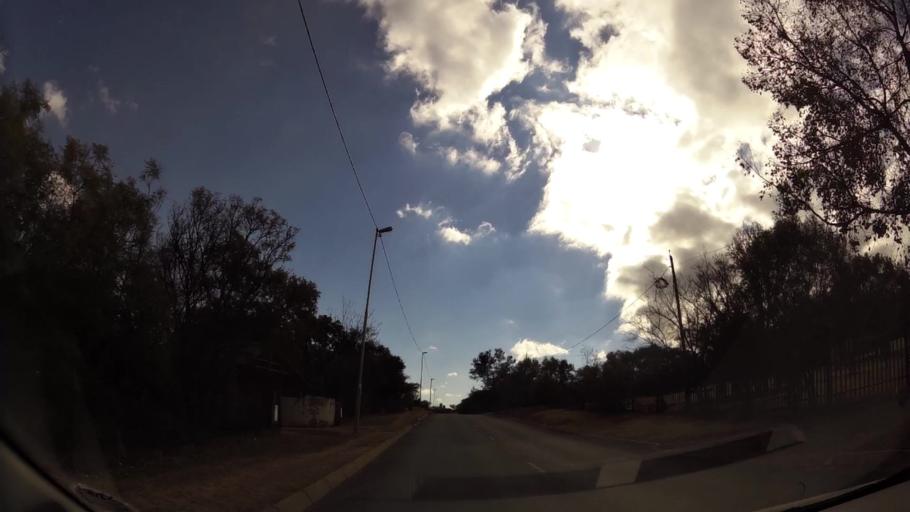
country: ZA
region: Gauteng
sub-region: West Rand District Municipality
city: Muldersdriseloop
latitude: -26.0844
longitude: 27.8541
